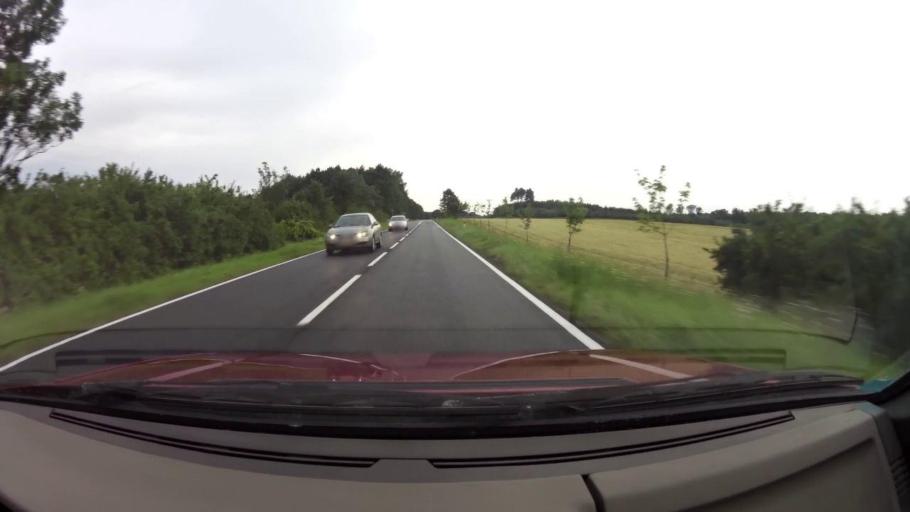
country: PL
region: West Pomeranian Voivodeship
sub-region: Powiat lobeski
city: Wegorzyno
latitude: 53.5168
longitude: 15.4981
